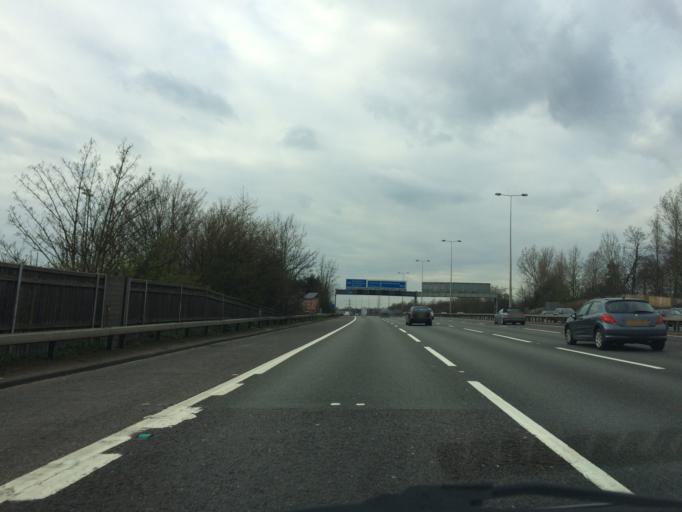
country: GB
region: England
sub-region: Surrey
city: Chertsey
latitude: 51.3822
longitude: -0.5157
